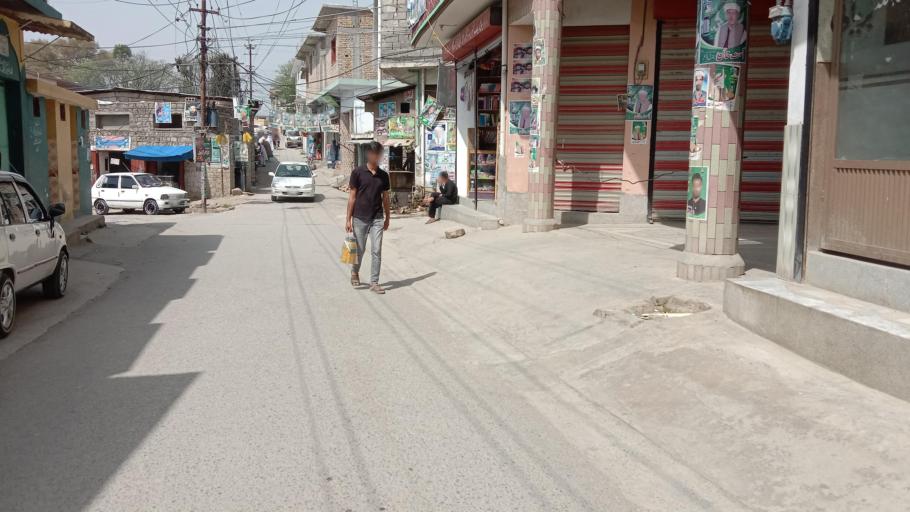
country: PK
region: Khyber Pakhtunkhwa
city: Abbottabad
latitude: 34.1650
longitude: 73.2628
